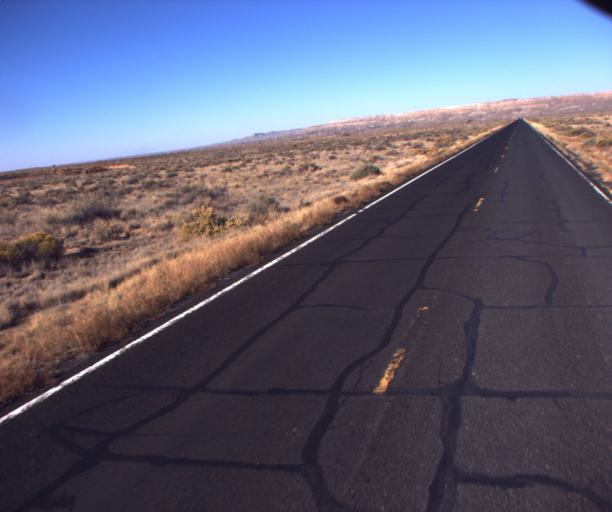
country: US
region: Arizona
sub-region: Navajo County
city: First Mesa
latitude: 35.8395
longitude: -110.3096
